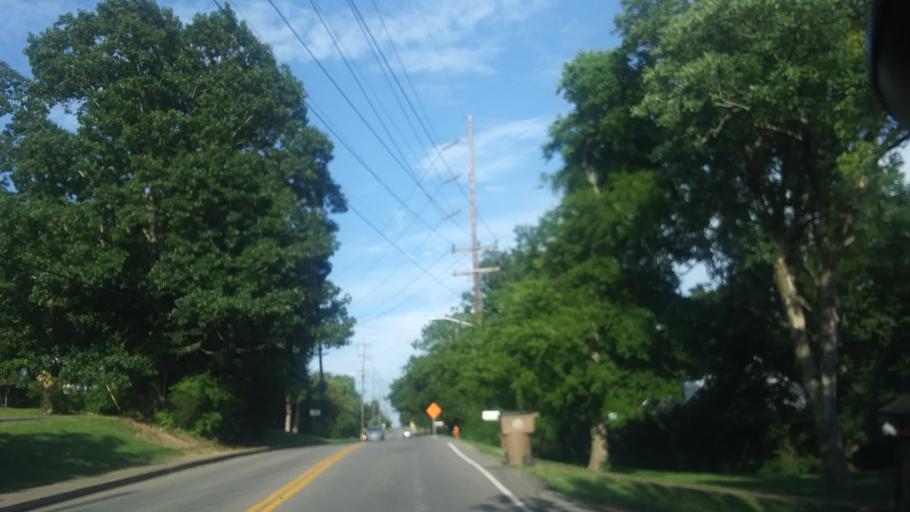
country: US
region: Tennessee
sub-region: Davidson County
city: Oak Hill
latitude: 36.0794
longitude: -86.7133
